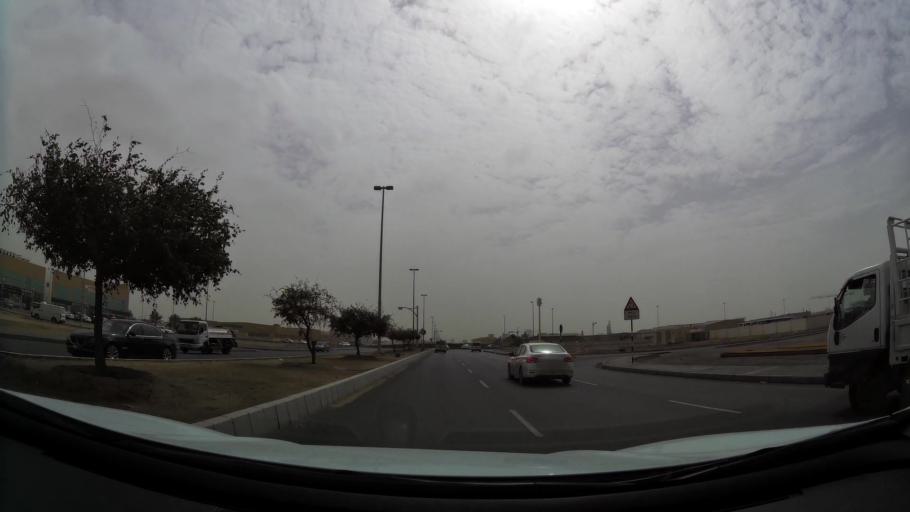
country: AE
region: Abu Dhabi
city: Abu Dhabi
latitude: 24.3458
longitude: 54.4726
